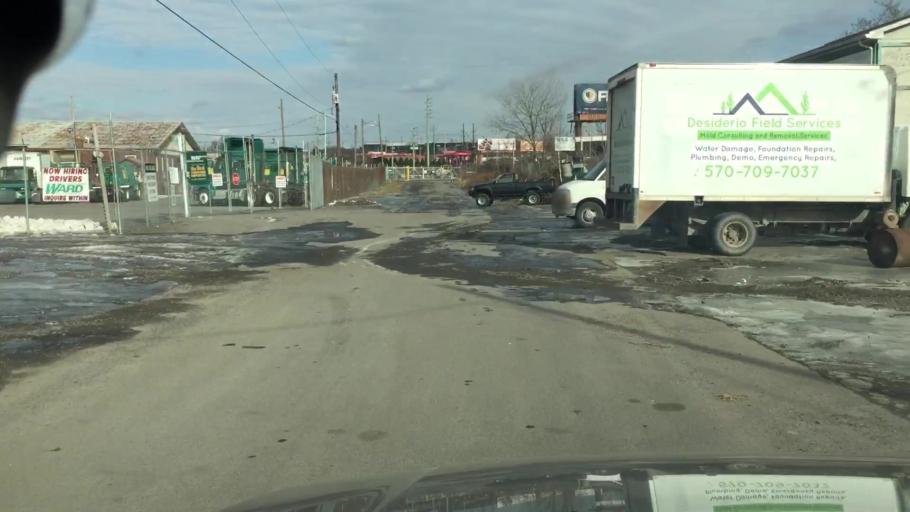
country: US
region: Pennsylvania
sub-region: Luzerne County
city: Georgetown
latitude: 41.2318
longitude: -75.8713
